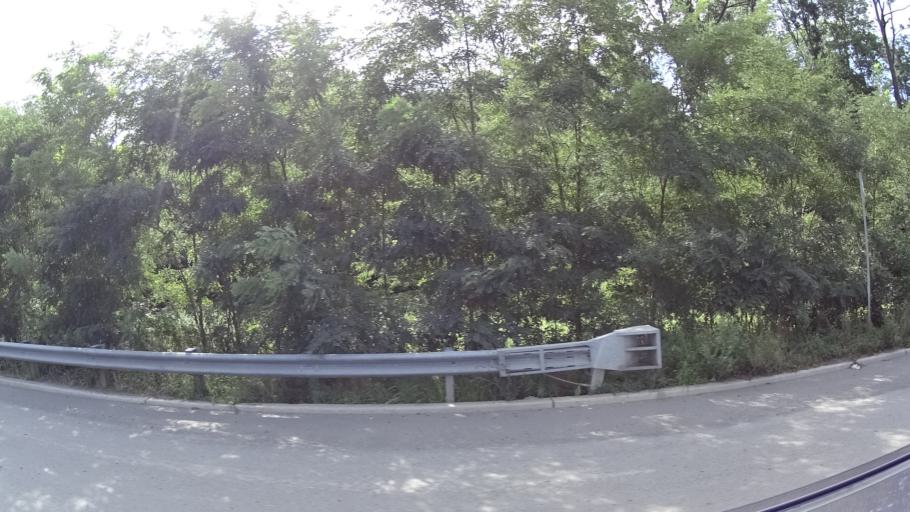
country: US
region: New Jersey
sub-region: Union County
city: Scotch Plains
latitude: 40.6563
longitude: -74.4040
